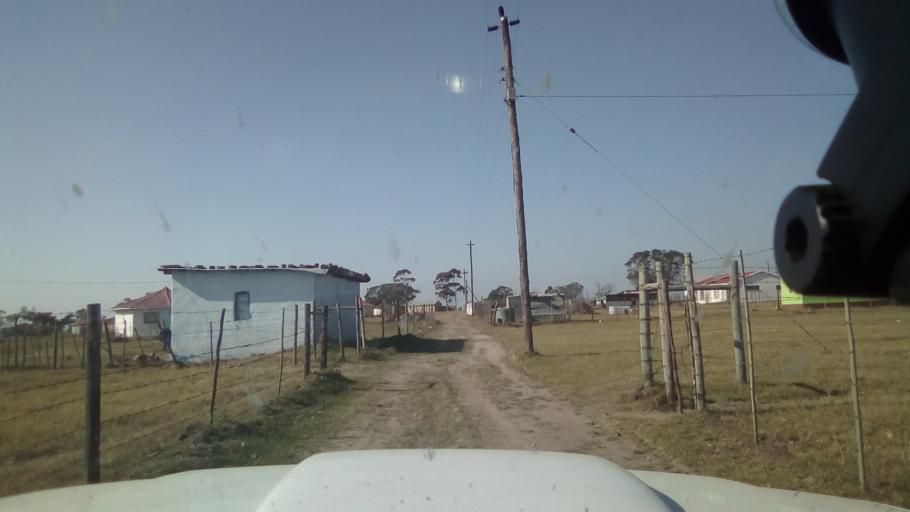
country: ZA
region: Eastern Cape
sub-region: Buffalo City Metropolitan Municipality
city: Bhisho
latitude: -32.9428
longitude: 27.3334
